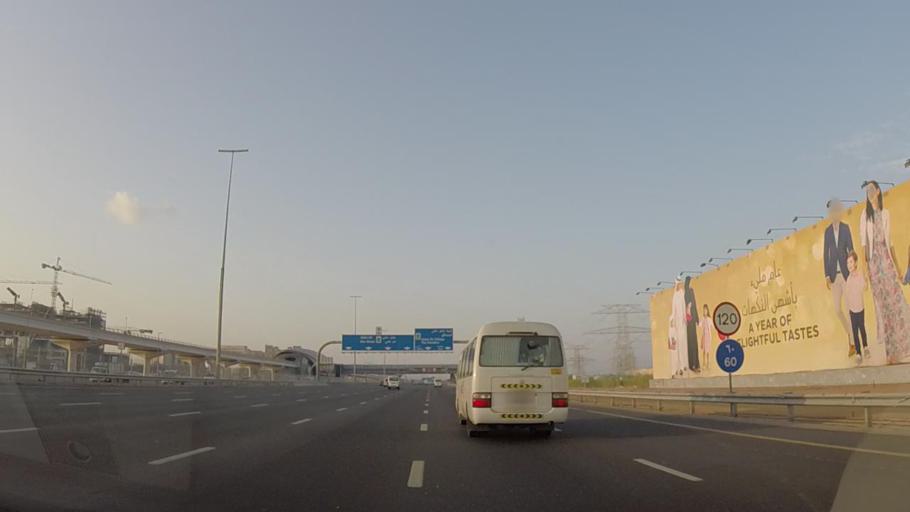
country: AE
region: Dubai
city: Dubai
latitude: 25.0436
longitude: 55.1139
